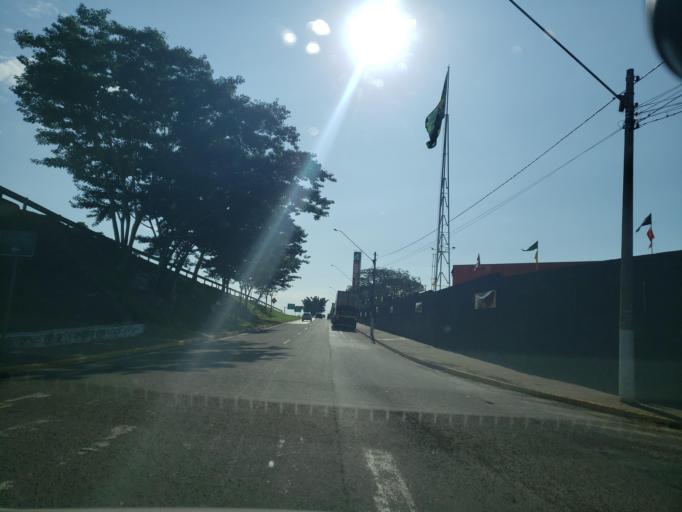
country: BR
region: Sao Paulo
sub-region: Aracatuba
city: Aracatuba
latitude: -21.2120
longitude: -50.4673
